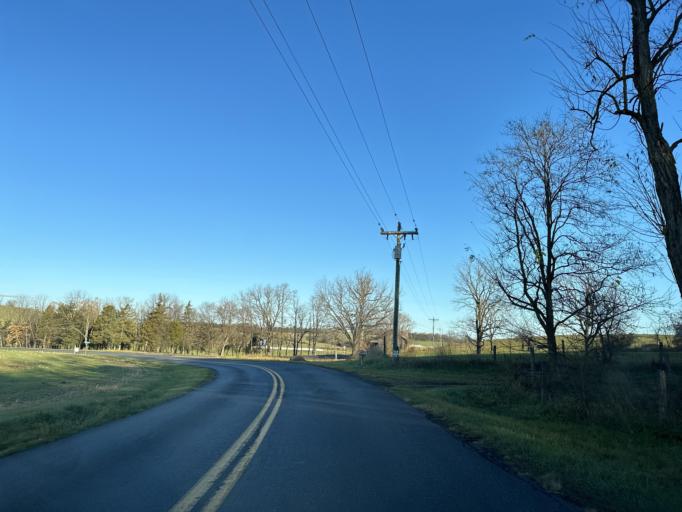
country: US
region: Virginia
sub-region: Rockingham County
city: Bridgewater
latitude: 38.3300
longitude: -78.9870
